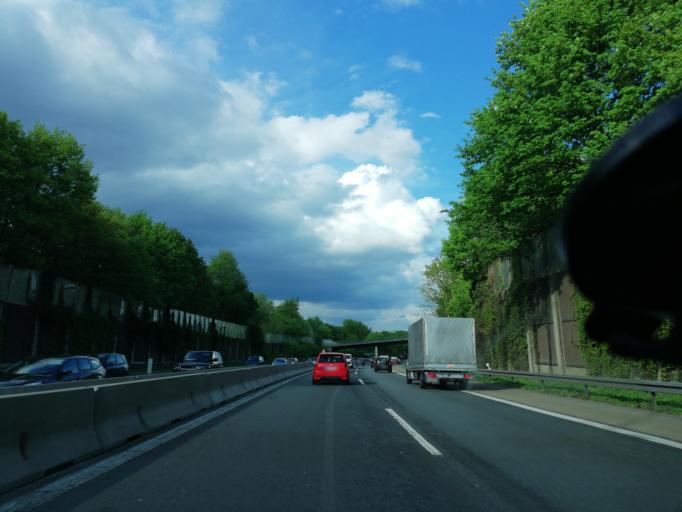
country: DE
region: North Rhine-Westphalia
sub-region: Regierungsbezirk Dusseldorf
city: Solingen
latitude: 51.2235
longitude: 7.0736
